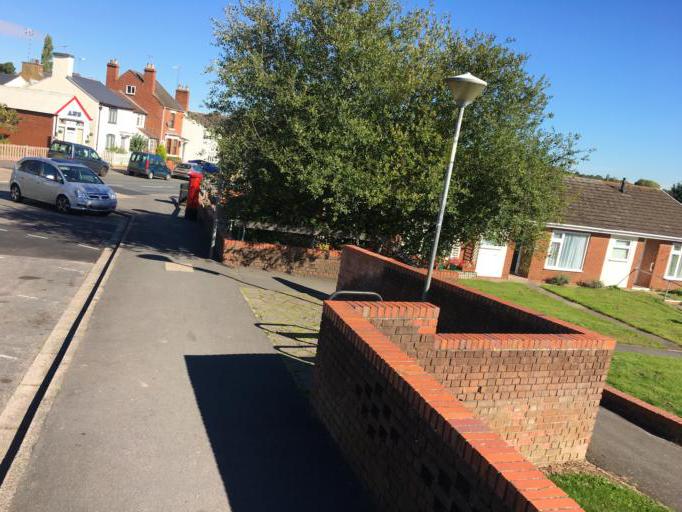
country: GB
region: England
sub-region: Warwickshire
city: Kenilworth
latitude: 52.3490
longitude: -1.5727
